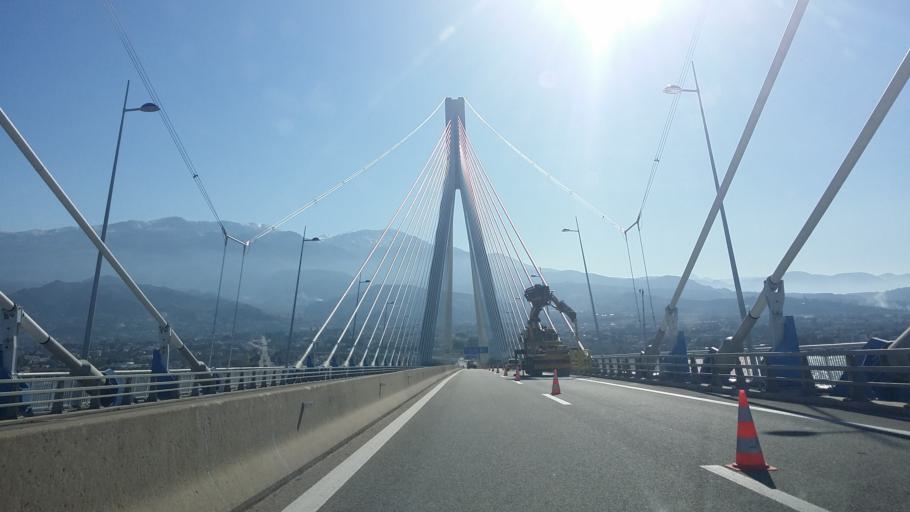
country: GR
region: West Greece
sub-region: Nomos Aitolias kai Akarnanias
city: Antirrio
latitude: 38.3165
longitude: 21.7757
